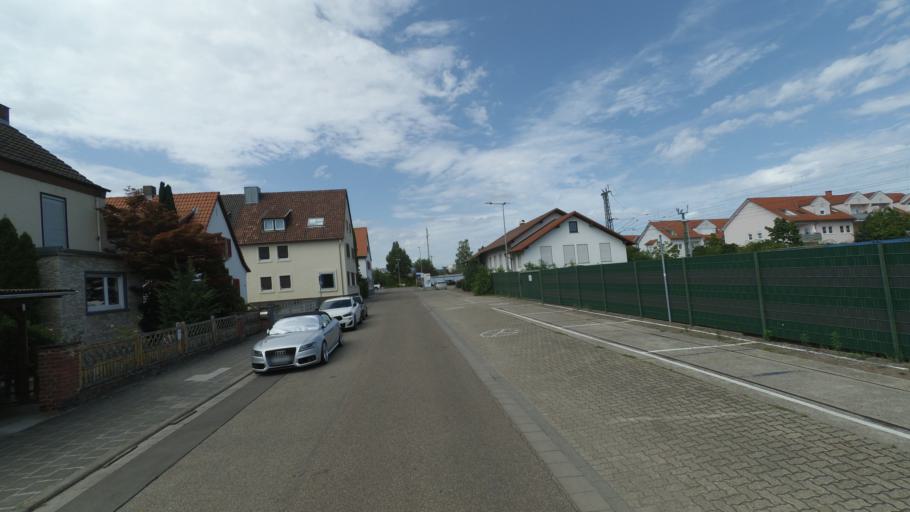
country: DE
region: Rheinland-Pfalz
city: Schifferstadt
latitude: 49.3884
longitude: 8.3629
